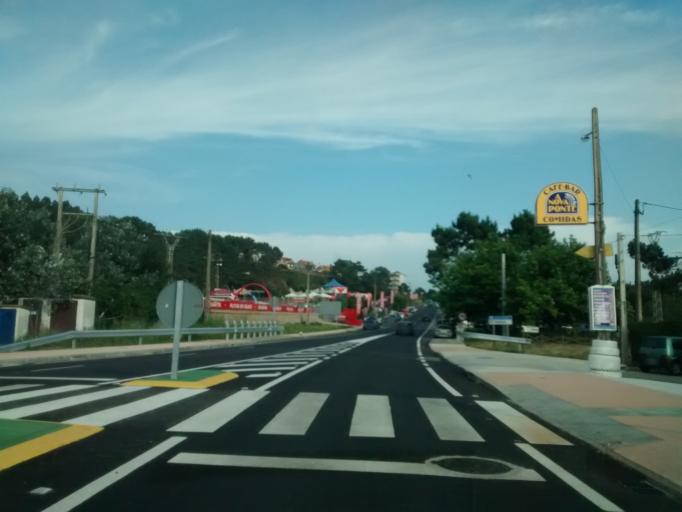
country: ES
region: Galicia
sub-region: Provincia de Pontevedra
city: Sanxenxo
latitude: 42.4164
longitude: -8.8681
